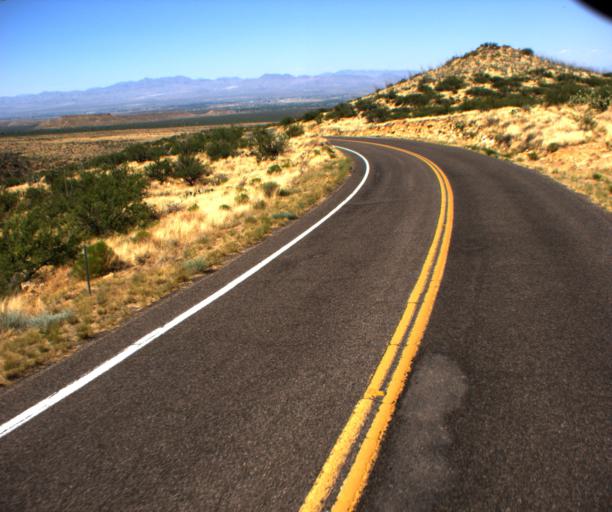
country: US
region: Arizona
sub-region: Graham County
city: Swift Trail Junction
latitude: 32.6865
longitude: -109.7651
